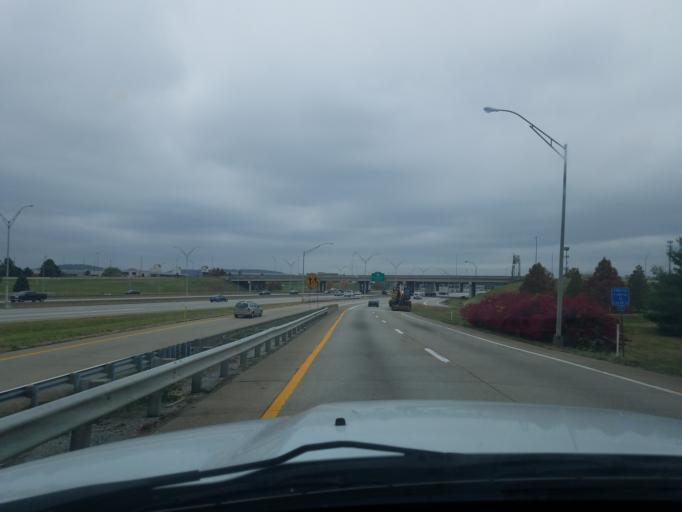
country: US
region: Kentucky
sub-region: Jefferson County
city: Audubon Park
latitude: 38.1905
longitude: -85.7358
